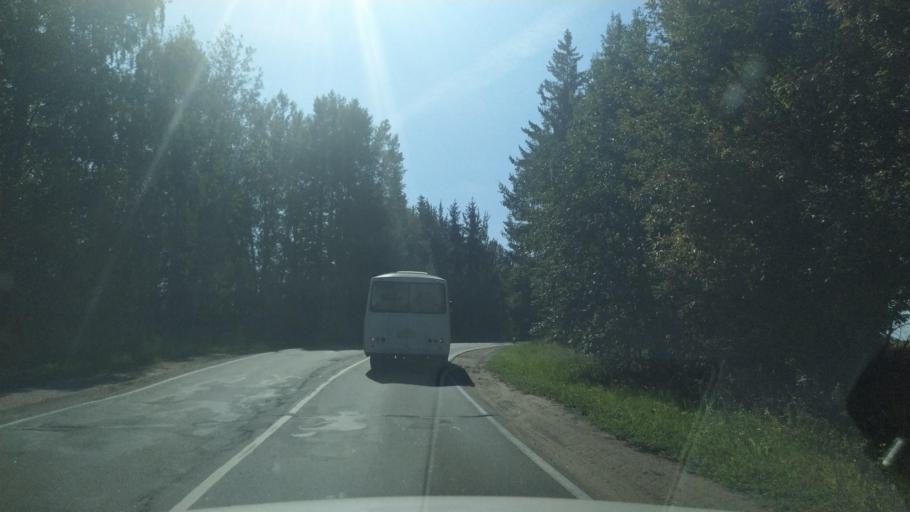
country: RU
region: Leningrad
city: Siverskiy
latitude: 59.3288
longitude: 30.0642
